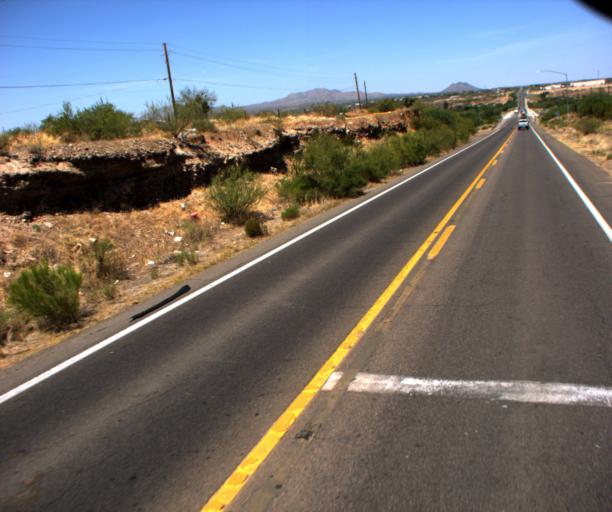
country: US
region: Arizona
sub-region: Gila County
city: Peridot
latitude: 33.2955
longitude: -110.4478
